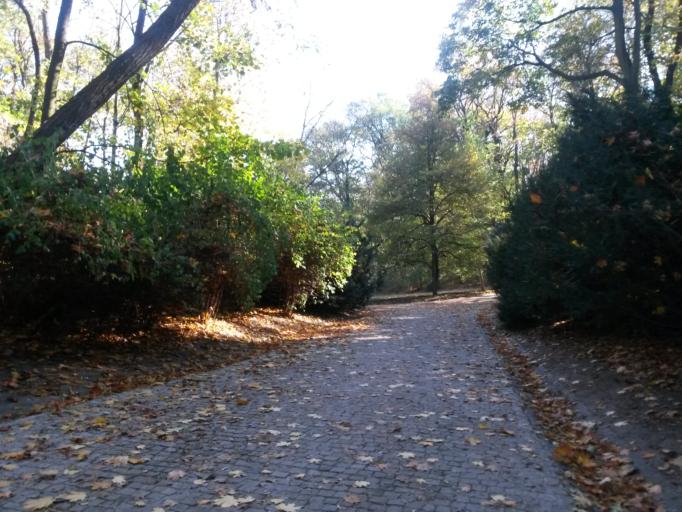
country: PL
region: Masovian Voivodeship
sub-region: Warszawa
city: Srodmiescie
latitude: 52.2161
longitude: 21.0278
